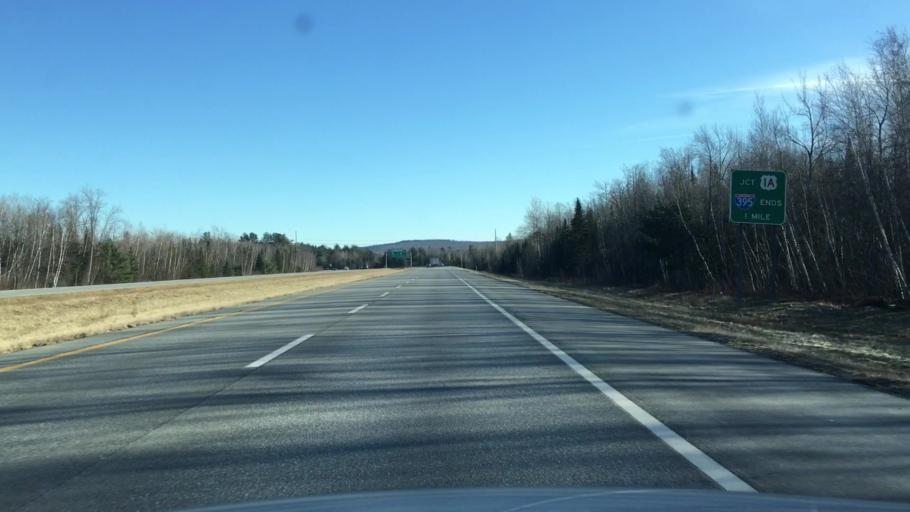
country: US
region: Maine
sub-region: Penobscot County
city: Brewer
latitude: 44.7708
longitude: -68.7402
